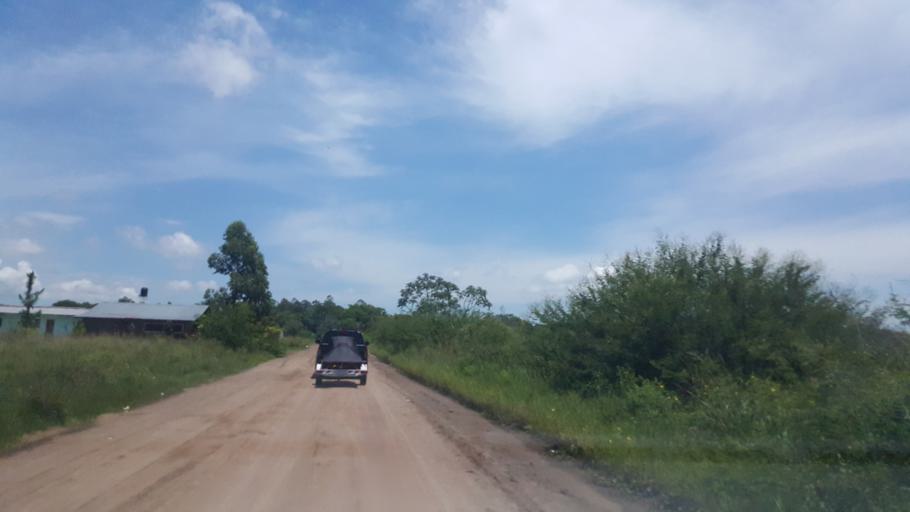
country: AR
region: Corrientes
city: Ituzaingo
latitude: -27.5995
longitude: -56.7060
